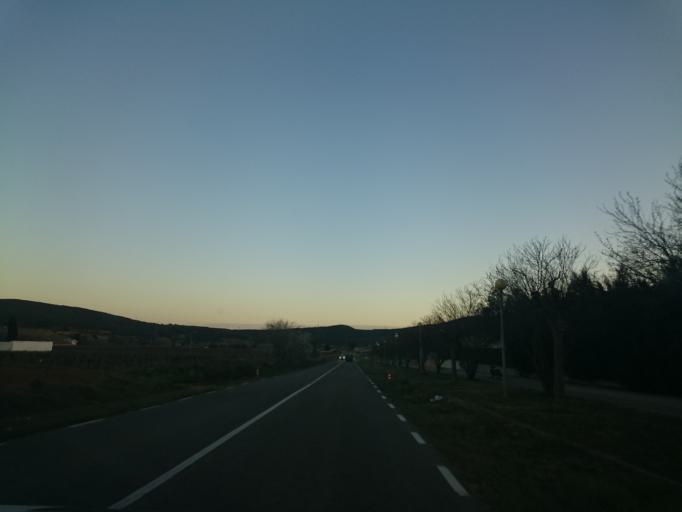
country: ES
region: Catalonia
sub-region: Provincia de Barcelona
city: La Granada
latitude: 41.3482
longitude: 1.7422
